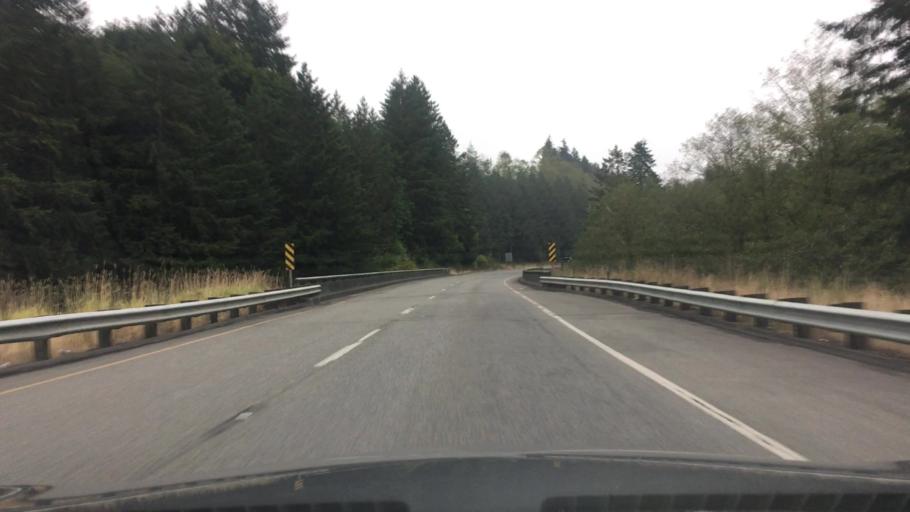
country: US
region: Washington
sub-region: Jefferson County
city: Port Hadlock-Irondale
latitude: 47.9525
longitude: -122.8840
